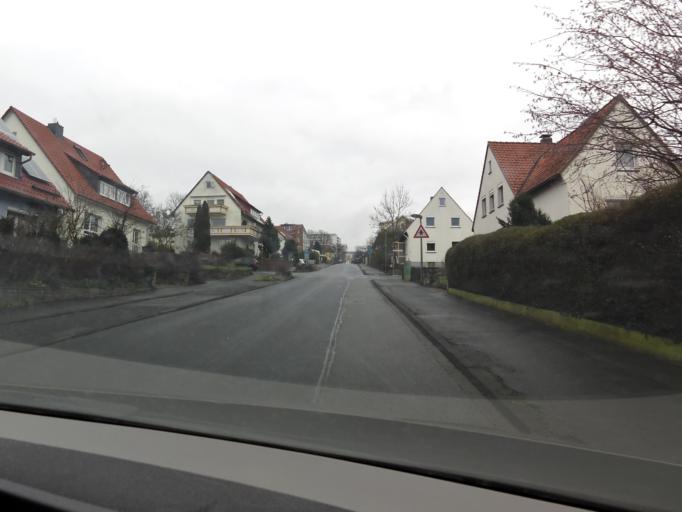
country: DE
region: Lower Saxony
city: Goettingen
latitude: 51.5142
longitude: 9.9618
